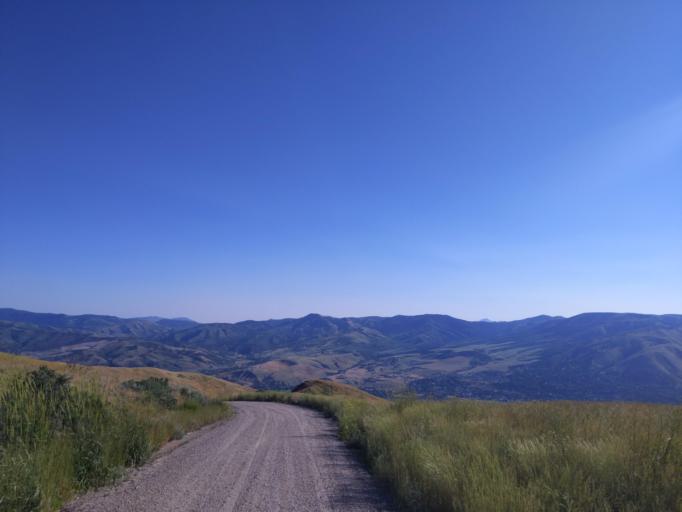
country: US
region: Idaho
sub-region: Bannock County
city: Pocatello
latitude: 42.8485
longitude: -112.3672
